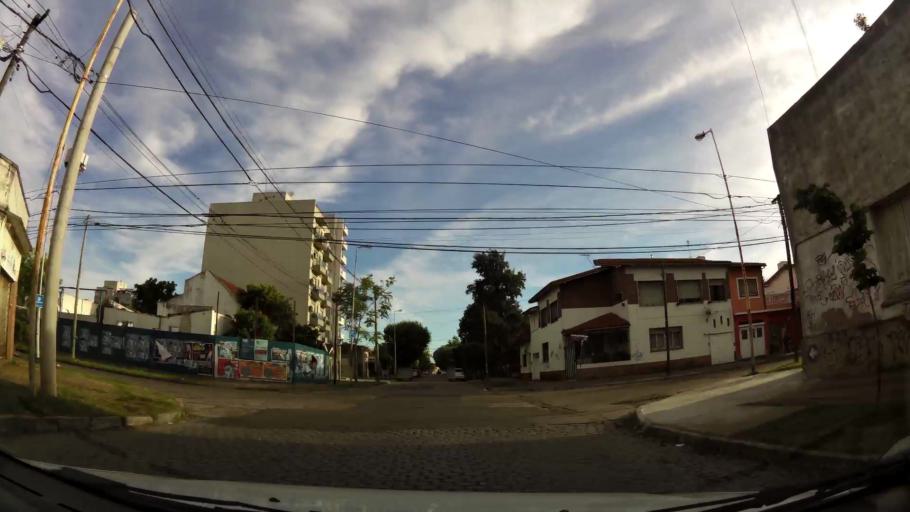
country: AR
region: Buenos Aires
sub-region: Partido de Moron
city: Moron
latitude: -34.6582
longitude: -58.6187
